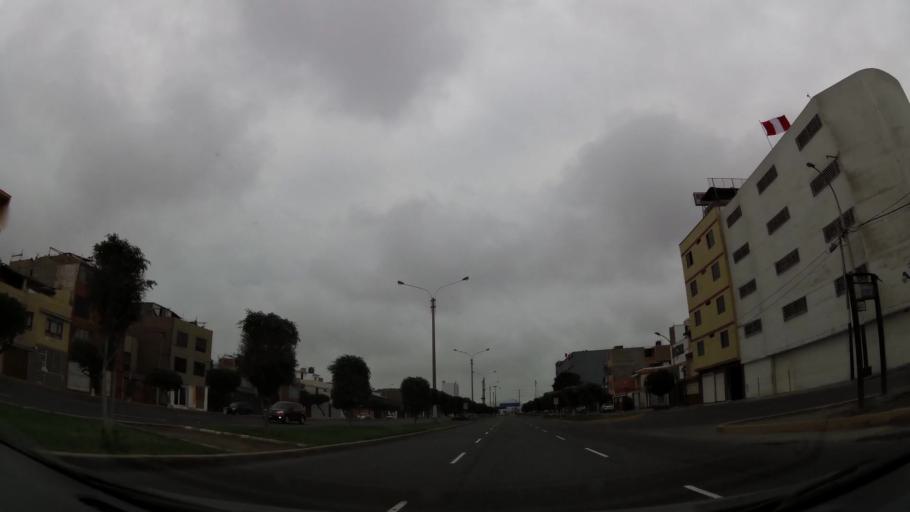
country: PE
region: Callao
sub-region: Callao
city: Callao
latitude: -12.0629
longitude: -77.1017
